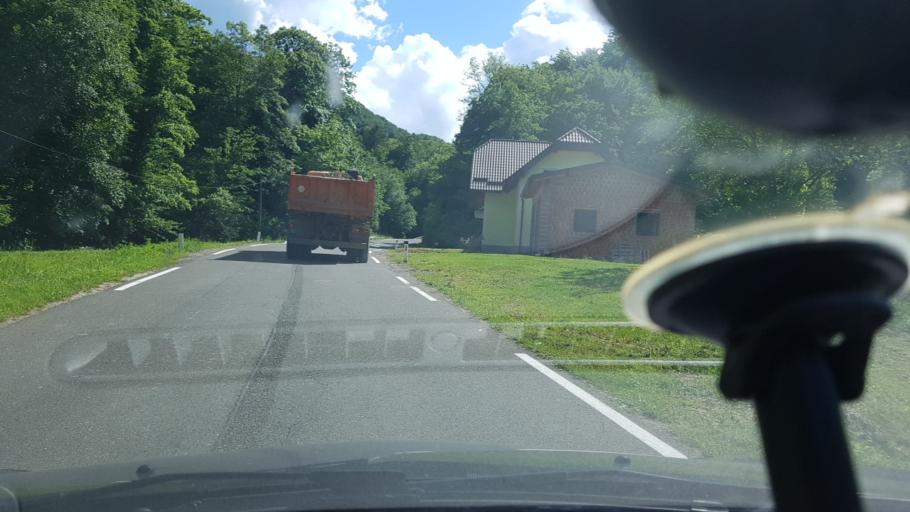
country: SI
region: Zetale
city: Zetale
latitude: 46.2644
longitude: 15.7686
